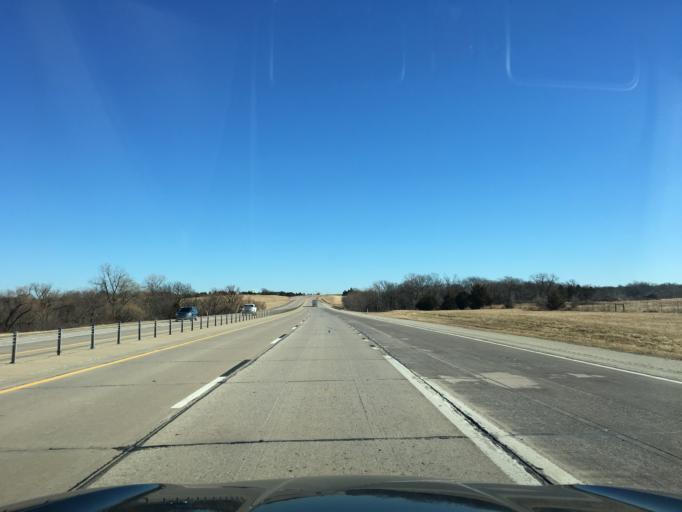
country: US
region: Oklahoma
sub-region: Payne County
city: Stillwater
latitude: 36.2400
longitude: -96.9431
